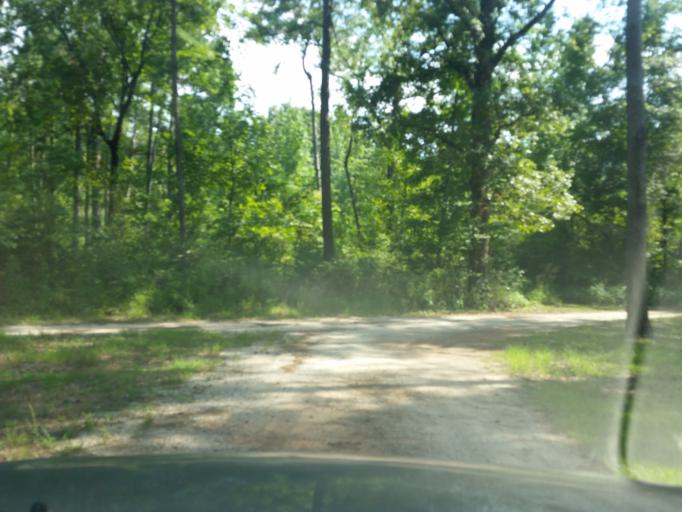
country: US
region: Alabama
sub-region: Baldwin County
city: Spanish Fort
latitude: 30.7450
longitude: -87.9164
